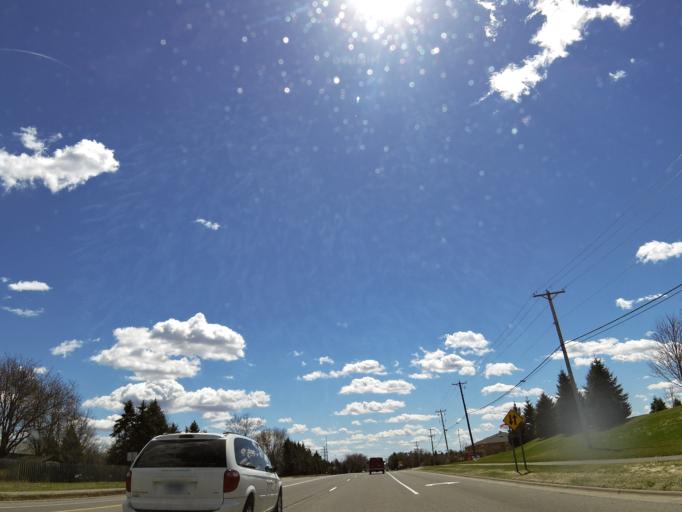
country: US
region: Minnesota
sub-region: Washington County
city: Cottage Grove
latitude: 44.8512
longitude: -92.9493
